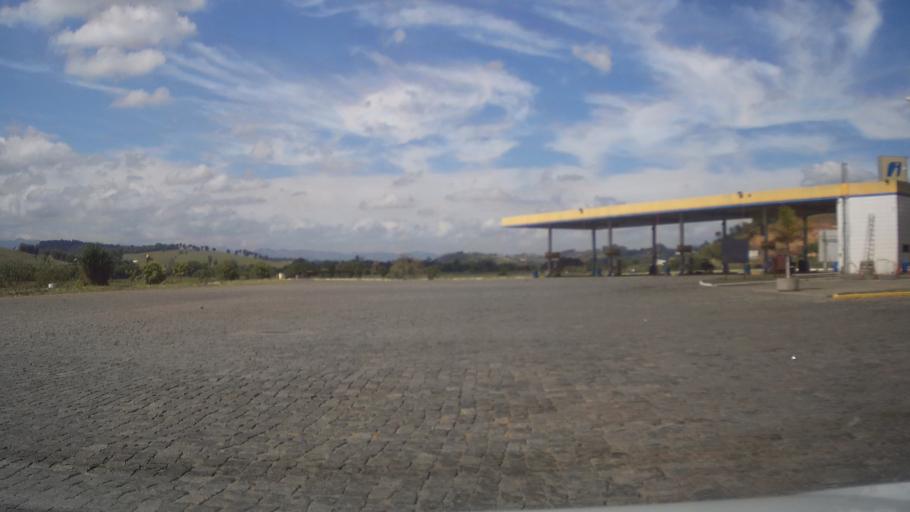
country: BR
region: Minas Gerais
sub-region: Cambui
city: Cambui
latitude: -22.5278
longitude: -46.0252
